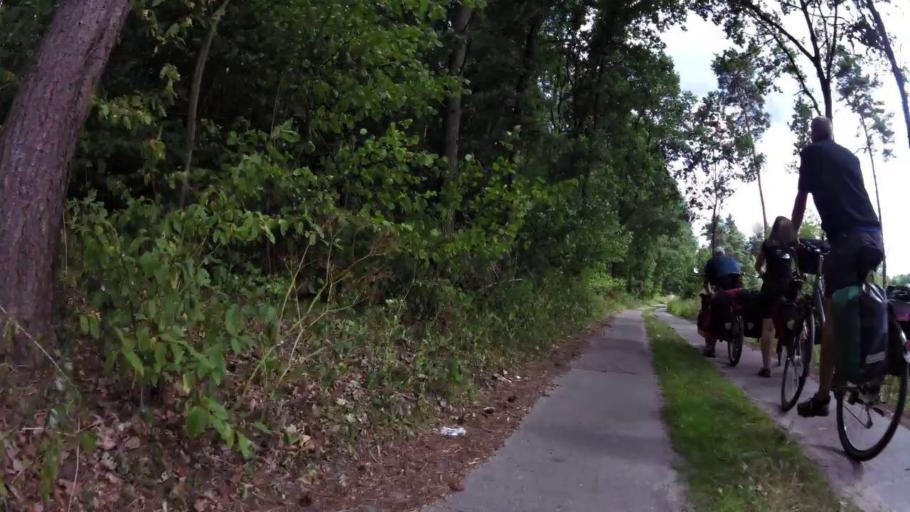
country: PL
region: West Pomeranian Voivodeship
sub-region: Powiat lobeski
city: Lobez
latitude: 53.6421
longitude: 15.5823
